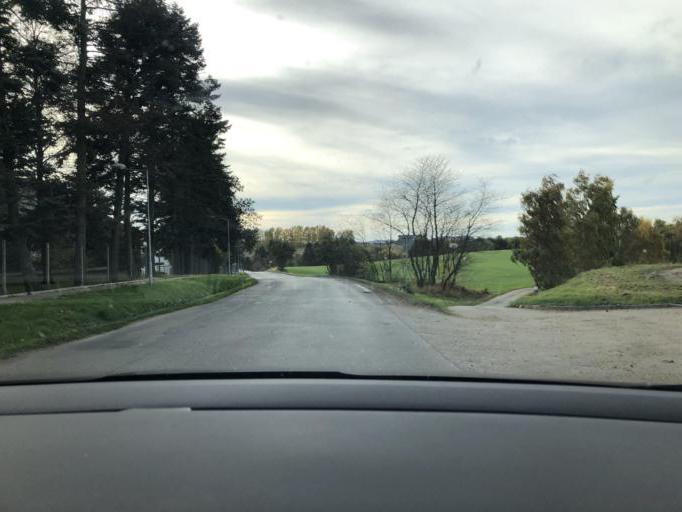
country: CZ
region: Central Bohemia
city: Postupice
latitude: 49.7654
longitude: 14.7578
